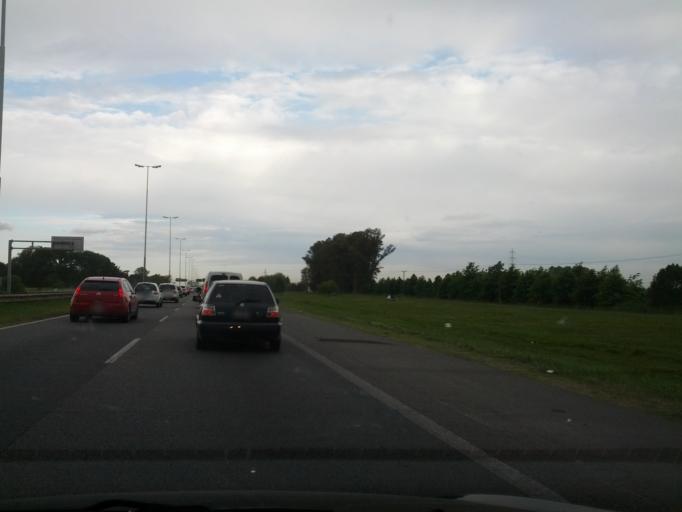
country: AR
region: Buenos Aires
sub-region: Partido de Lujan
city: Lujan
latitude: -34.5703
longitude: -59.0531
